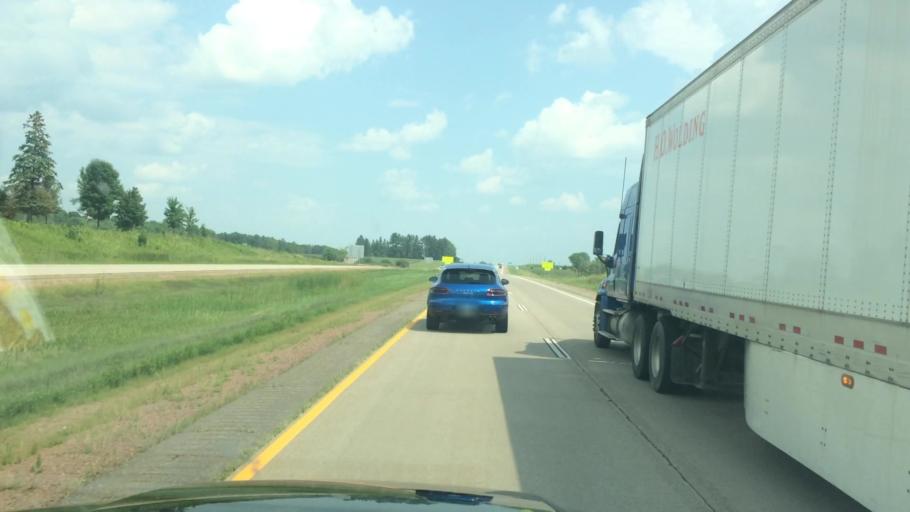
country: US
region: Wisconsin
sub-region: Clark County
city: Abbotsford
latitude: 44.9458
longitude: -90.2729
